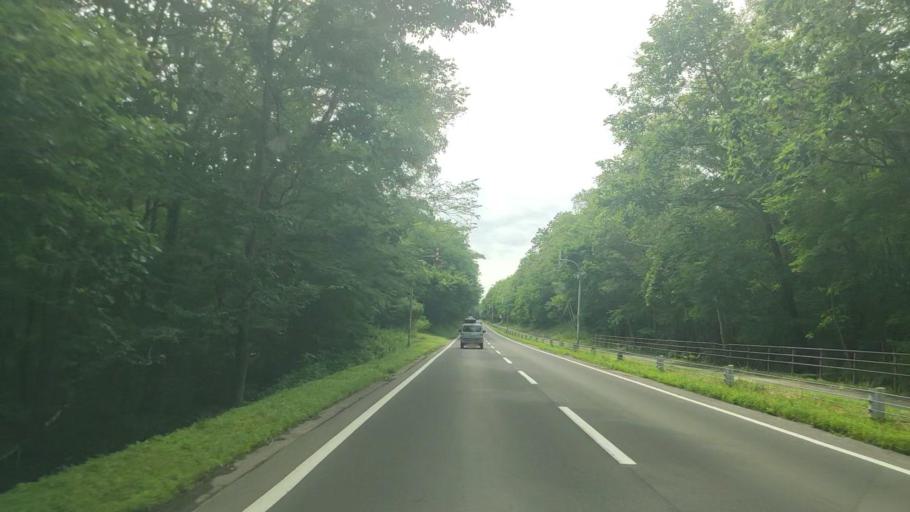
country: JP
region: Hokkaido
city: Chitose
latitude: 42.7942
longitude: 141.5587
